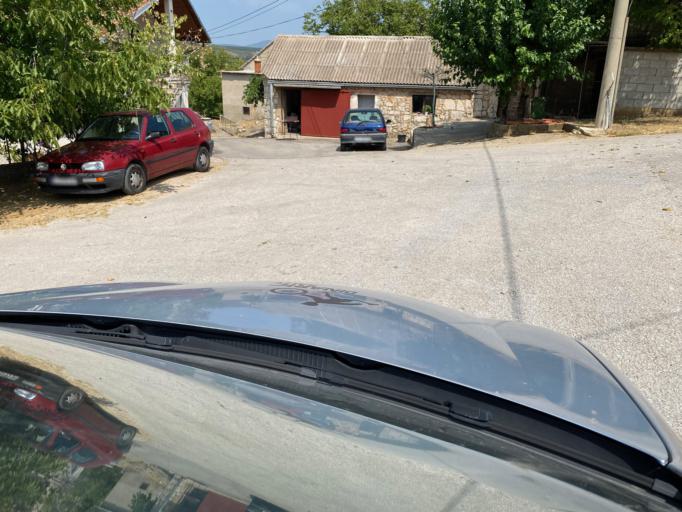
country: BA
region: Federation of Bosnia and Herzegovina
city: Bosansko Grahovo
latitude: 43.9498
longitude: 16.4386
